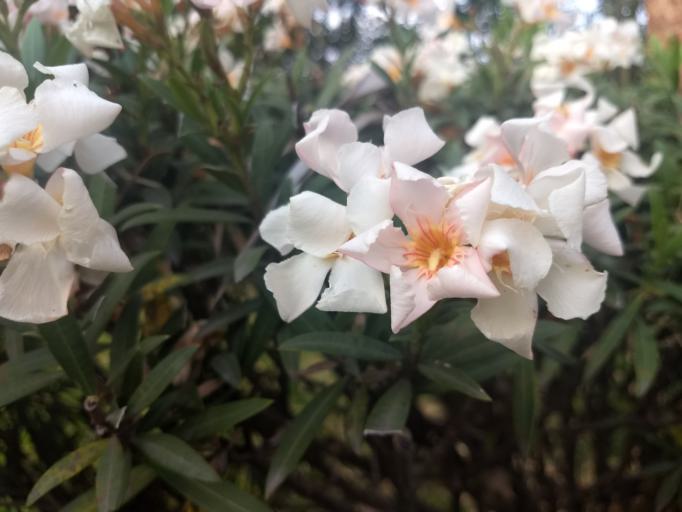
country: MX
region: Nuevo Leon
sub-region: Monterrey
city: Monterrey
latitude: 25.6736
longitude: -100.2906
